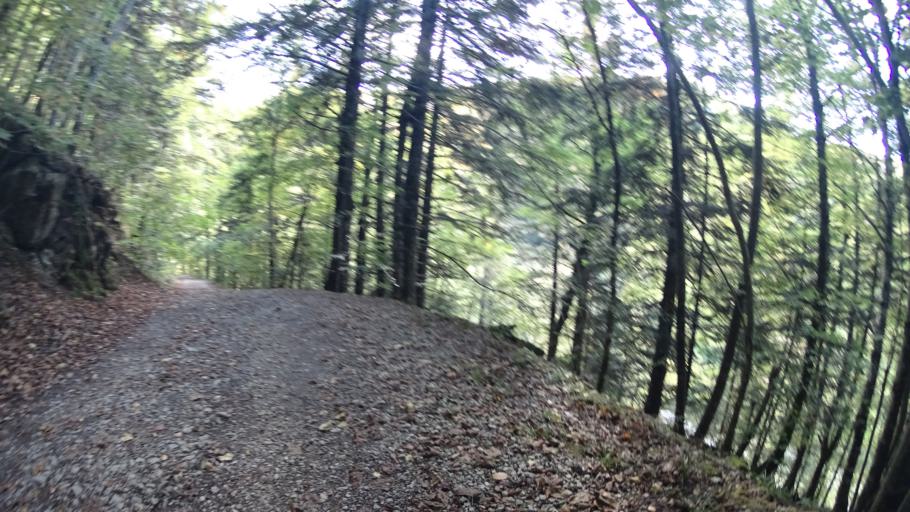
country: ES
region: Navarre
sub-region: Provincia de Navarra
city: Oronz
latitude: 42.9826
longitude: -1.1211
